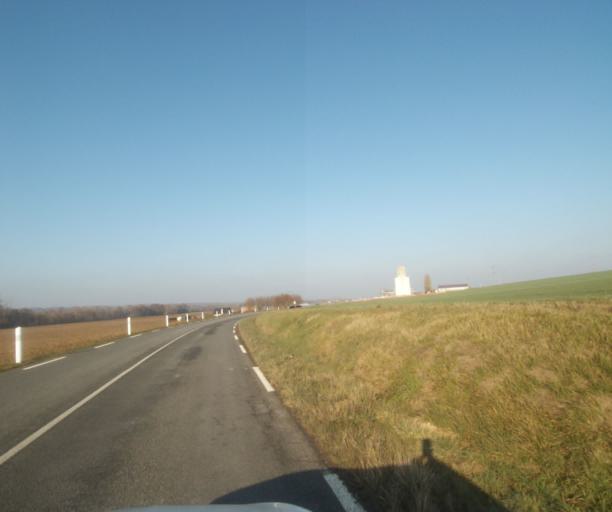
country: FR
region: Champagne-Ardenne
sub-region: Departement de la Haute-Marne
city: Wassy
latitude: 48.5099
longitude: 4.9389
